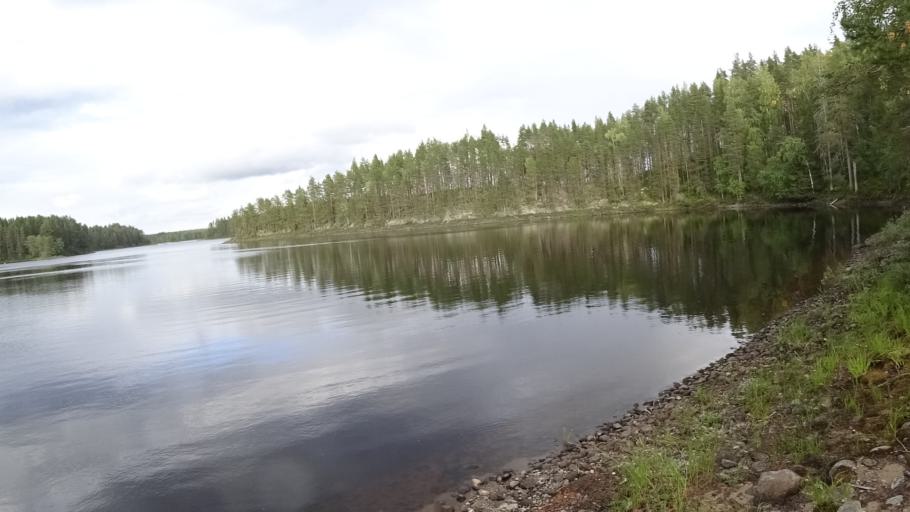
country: FI
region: North Karelia
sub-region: Joensuu
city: Ilomantsi
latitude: 62.5733
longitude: 31.1734
